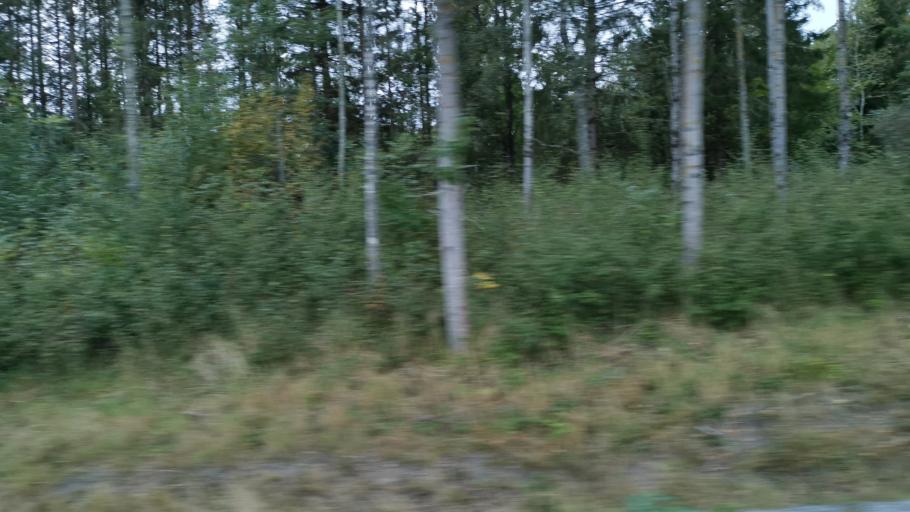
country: SE
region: Vaestra Goetaland
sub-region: Tanums Kommun
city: Tanumshede
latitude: 58.6908
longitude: 11.3351
